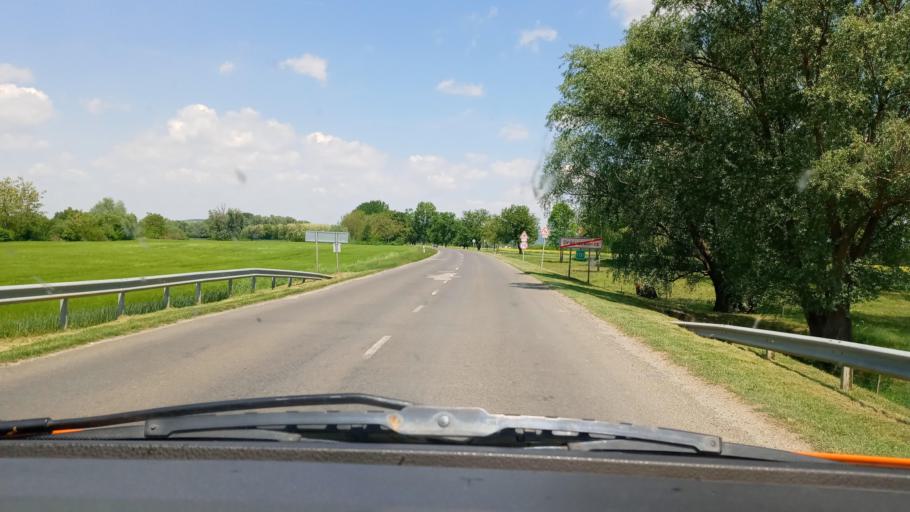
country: HU
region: Baranya
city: Harkany
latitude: 45.8099
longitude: 18.2131
